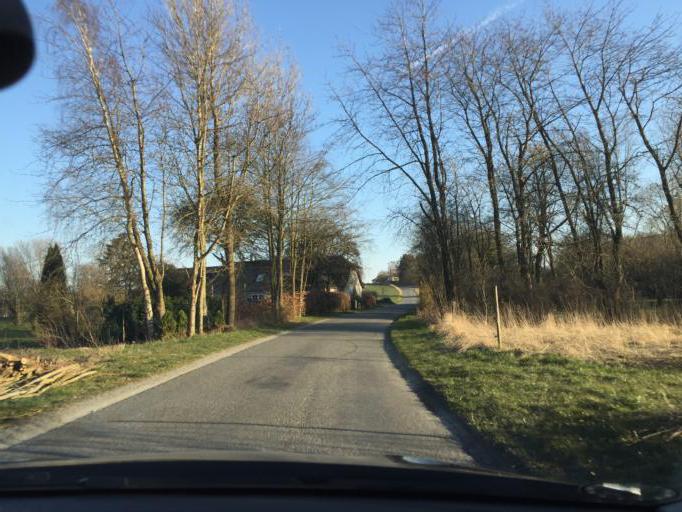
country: DK
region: South Denmark
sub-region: Faaborg-Midtfyn Kommune
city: Arslev
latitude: 55.2928
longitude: 10.4737
